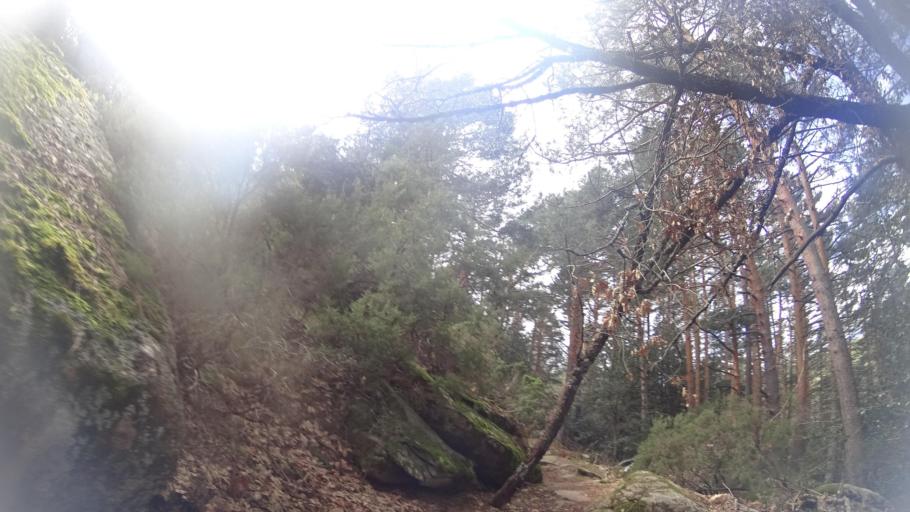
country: ES
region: Madrid
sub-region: Provincia de Madrid
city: Canencia
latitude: 40.8718
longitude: -3.7801
